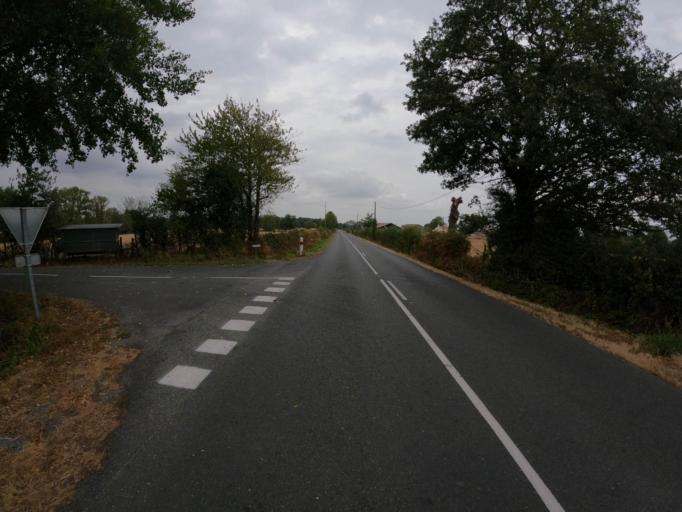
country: FR
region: Pays de la Loire
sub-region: Departement de Maine-et-Loire
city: Le Longeron
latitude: 47.0375
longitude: -1.0380
